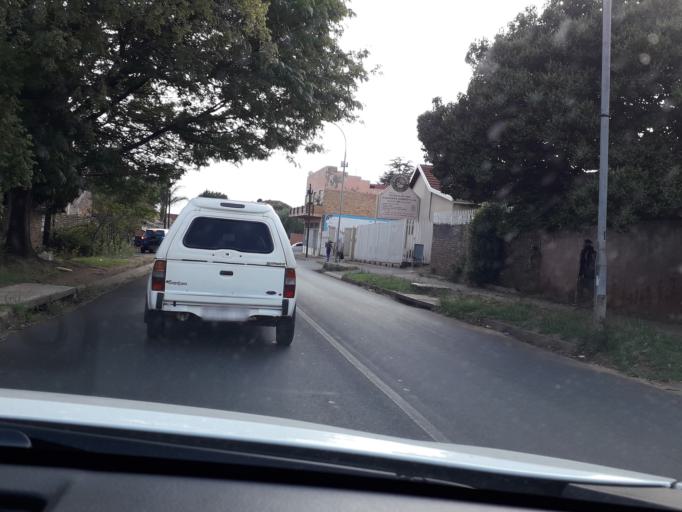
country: ZA
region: Gauteng
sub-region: City of Johannesburg Metropolitan Municipality
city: Johannesburg
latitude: -26.1666
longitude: 27.9768
